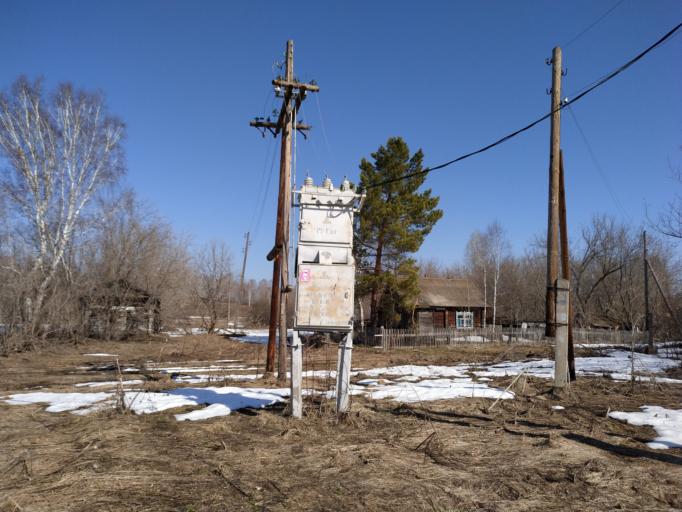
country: RU
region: Altai Krai
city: Krasnogorskoye
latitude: 52.4896
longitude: 86.2397
